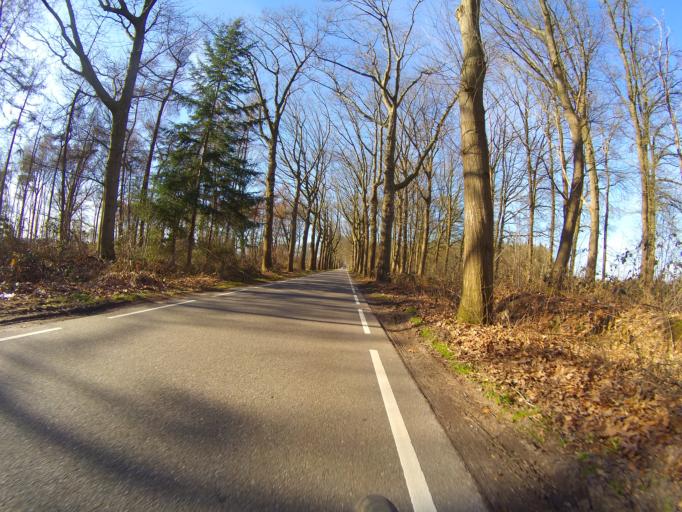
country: NL
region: Utrecht
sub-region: Gemeente Leusden
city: Leusden
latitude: 52.1020
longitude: 5.4644
